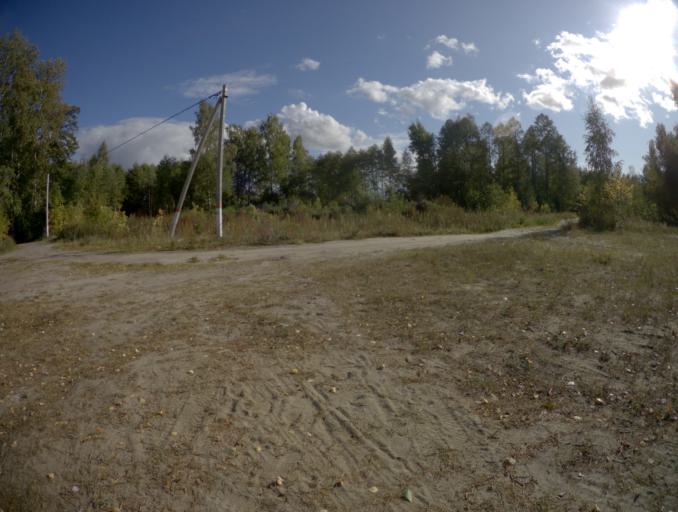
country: RU
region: Moskovskaya
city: Kerva
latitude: 55.6100
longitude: 39.5690
